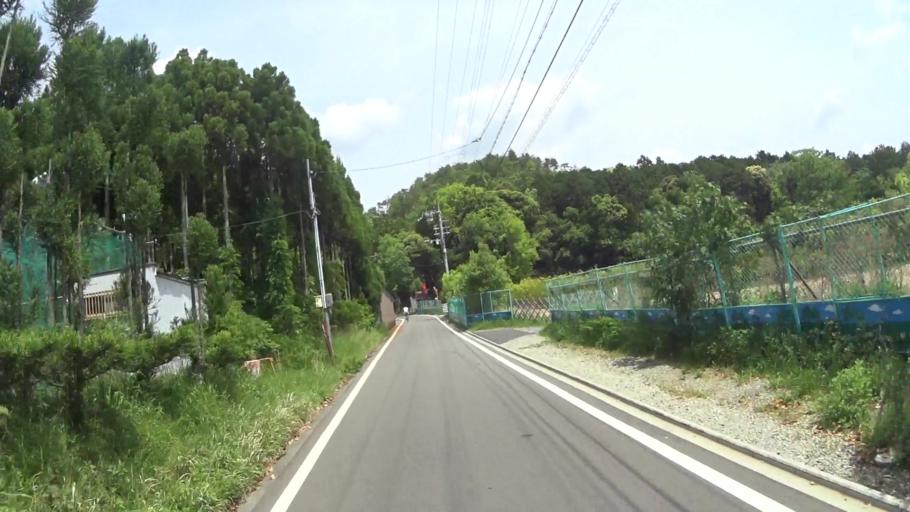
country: JP
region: Kyoto
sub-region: Kyoto-shi
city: Kamigyo-ku
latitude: 35.0559
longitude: 135.7292
